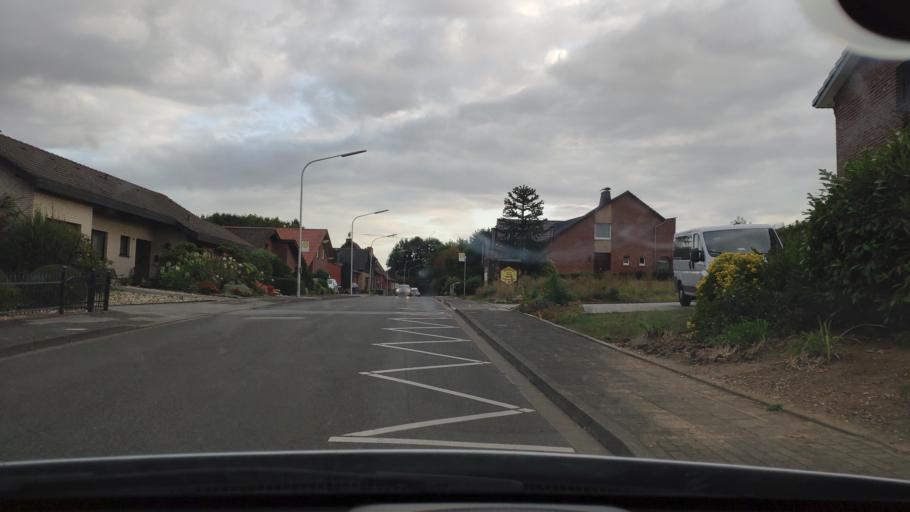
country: DE
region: North Rhine-Westphalia
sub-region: Regierungsbezirk Koln
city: Heinsberg
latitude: 51.0530
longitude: 6.1245
